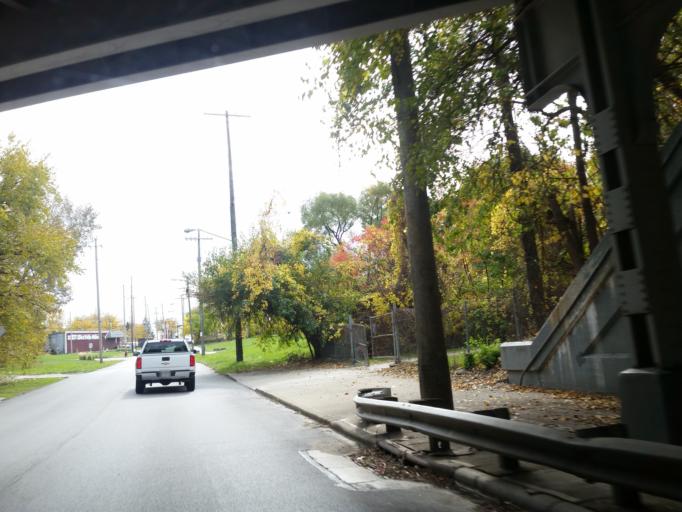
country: US
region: Ohio
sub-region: Cuyahoga County
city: Newburgh Heights
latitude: 41.4810
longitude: -81.6364
